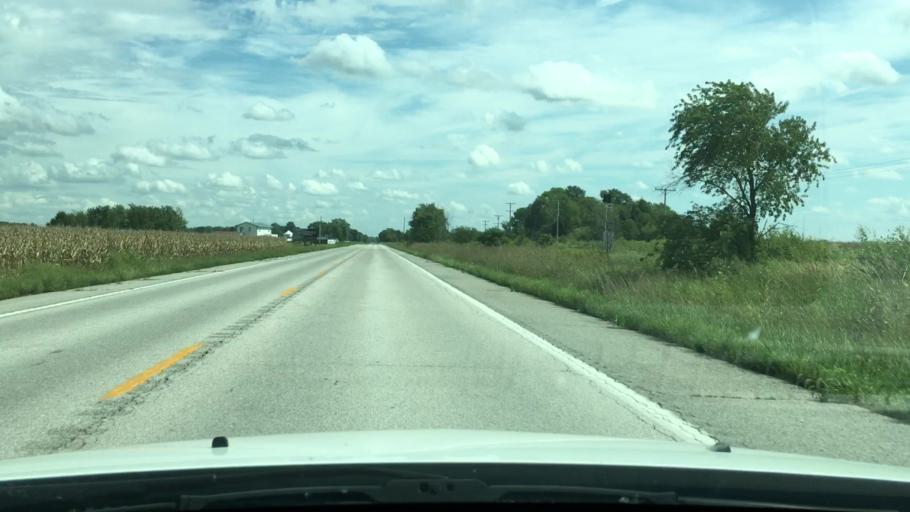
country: US
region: Missouri
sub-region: Audrain County
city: Vandalia
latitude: 39.2906
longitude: -91.5341
